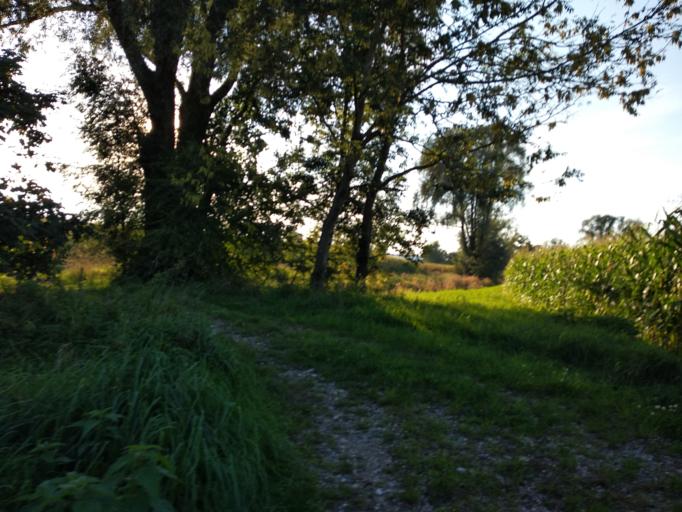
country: DE
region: Bavaria
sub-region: Upper Bavaria
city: Steinhoring
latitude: 48.0892
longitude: 12.0450
